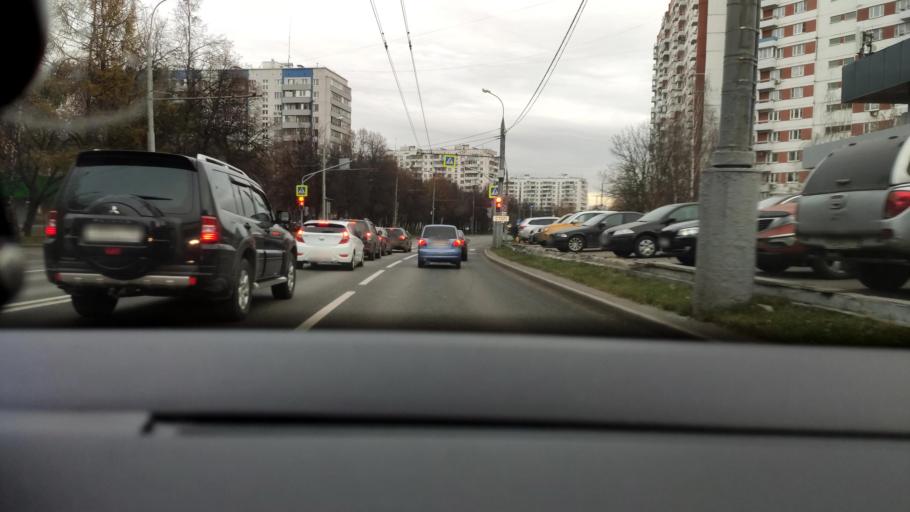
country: RU
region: Moscow
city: Strogino
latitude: 55.8505
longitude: 37.4110
